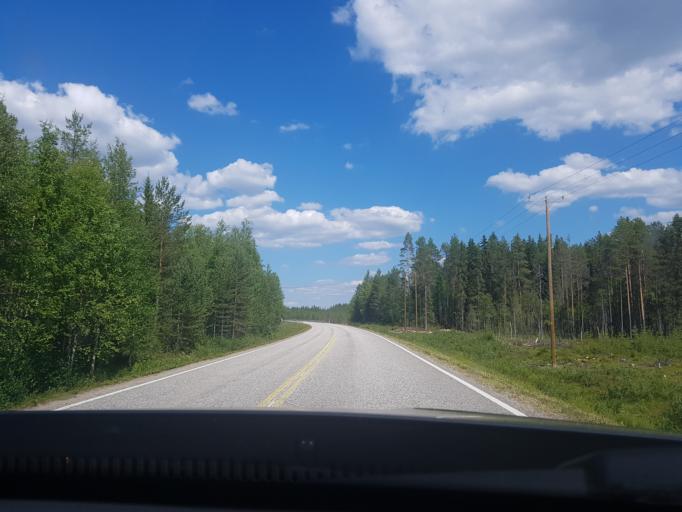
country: FI
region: Kainuu
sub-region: Kehys-Kainuu
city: Kuhmo
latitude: 64.2204
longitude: 29.7964
